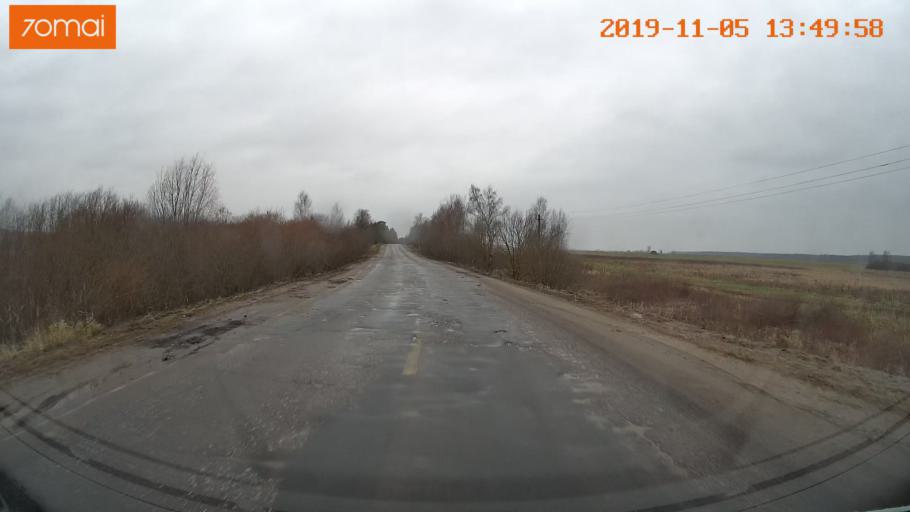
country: RU
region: Ivanovo
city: Kaminskiy
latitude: 57.0156
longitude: 41.4105
